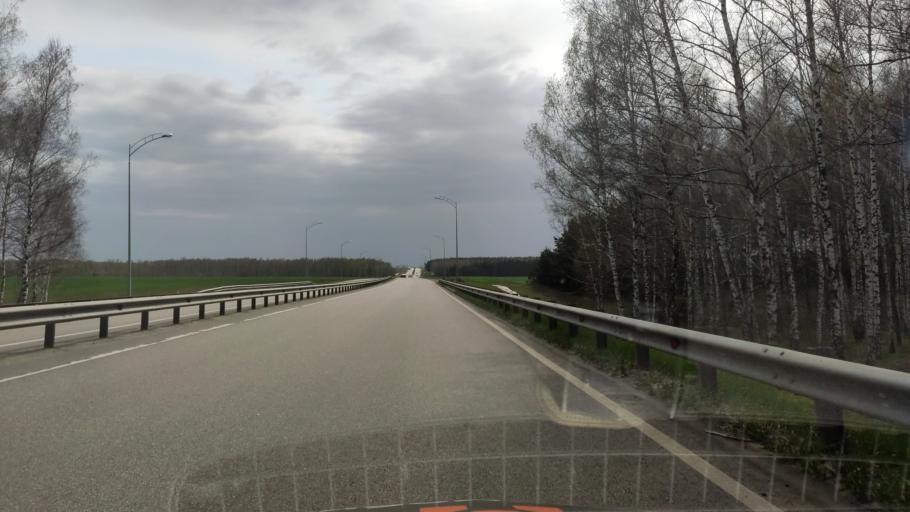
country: RU
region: Belgorod
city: Staryy Oskol
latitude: 51.4086
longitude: 37.8820
